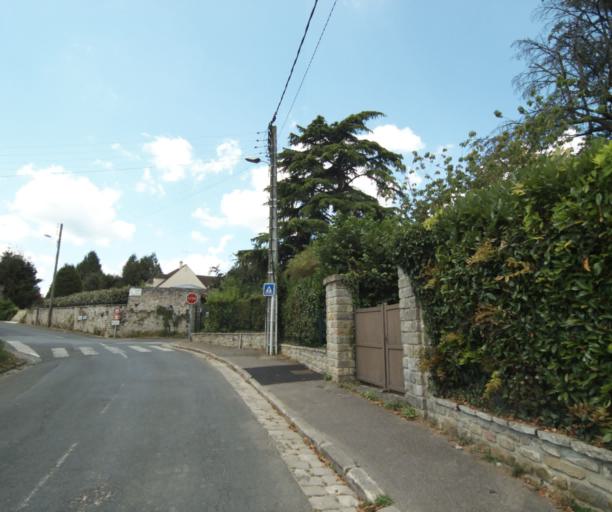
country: FR
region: Ile-de-France
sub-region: Departement de Seine-et-Marne
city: Samois-sur-Seine
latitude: 48.4535
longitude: 2.7530
